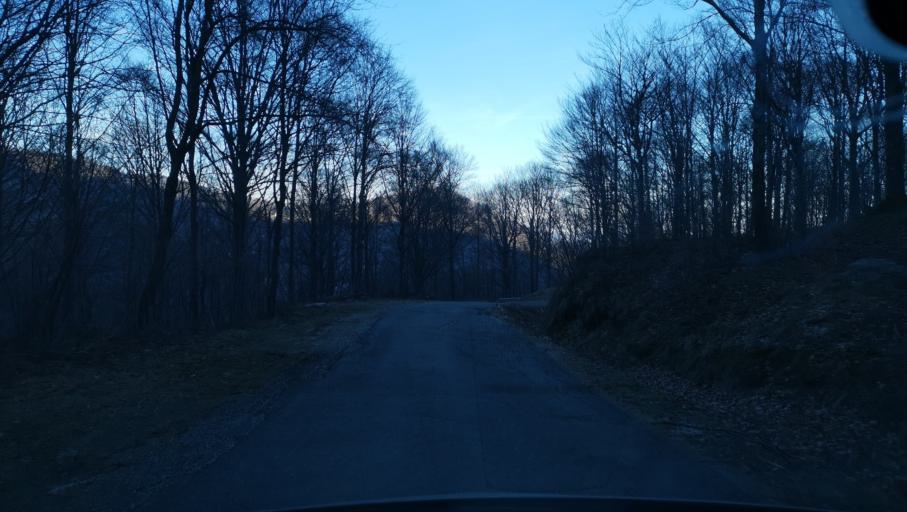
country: IT
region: Piedmont
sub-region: Provincia di Torino
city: Rora
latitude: 44.7819
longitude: 7.1923
